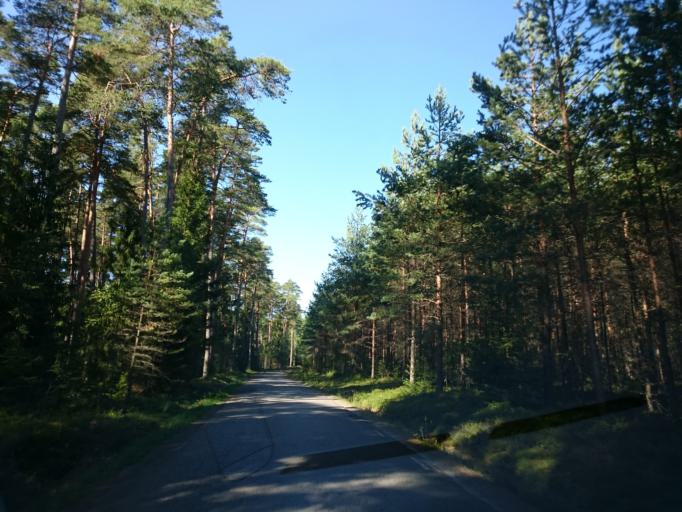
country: SE
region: Soedermanland
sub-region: Nykopings Kommun
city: Stigtomta
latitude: 58.6376
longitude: 16.6950
